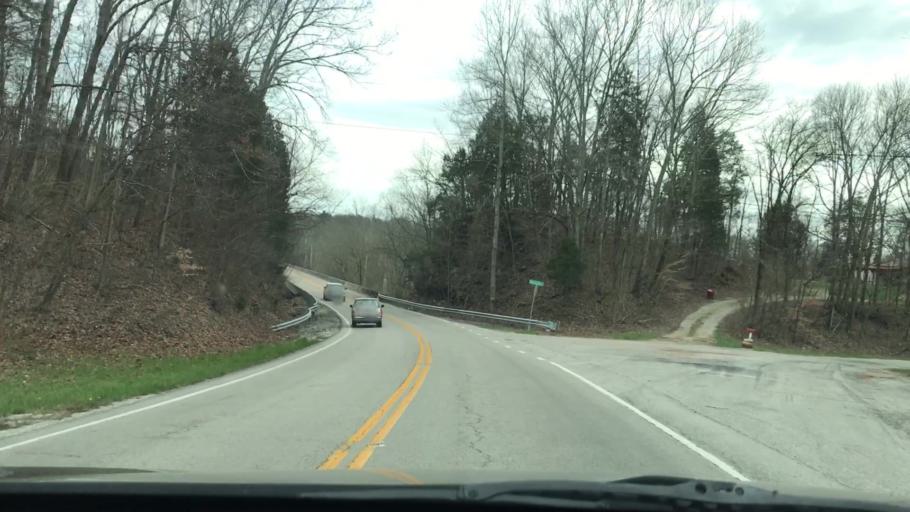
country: US
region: Kentucky
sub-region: Hart County
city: Munfordville
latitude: 37.3211
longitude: -85.7642
